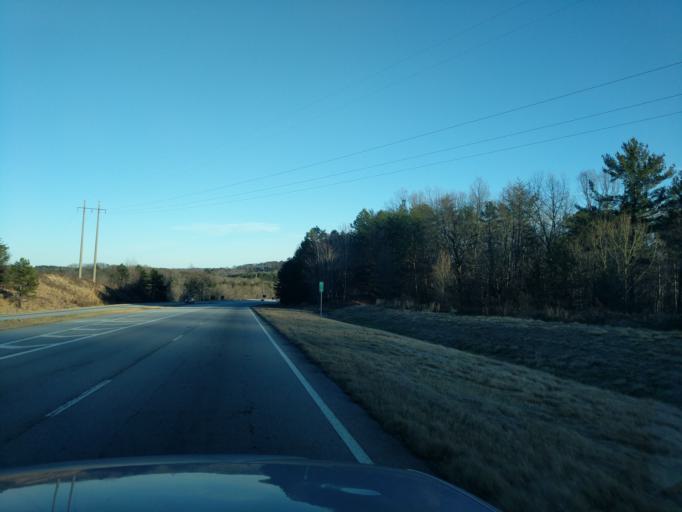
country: US
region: Georgia
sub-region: Stephens County
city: Toccoa
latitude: 34.5533
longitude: -83.3767
